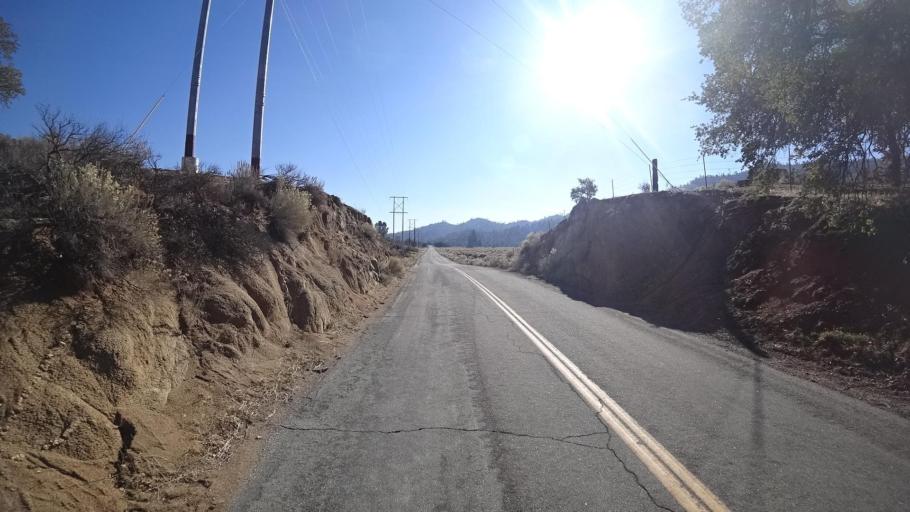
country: US
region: California
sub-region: Kern County
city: Bodfish
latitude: 35.3941
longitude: -118.4355
